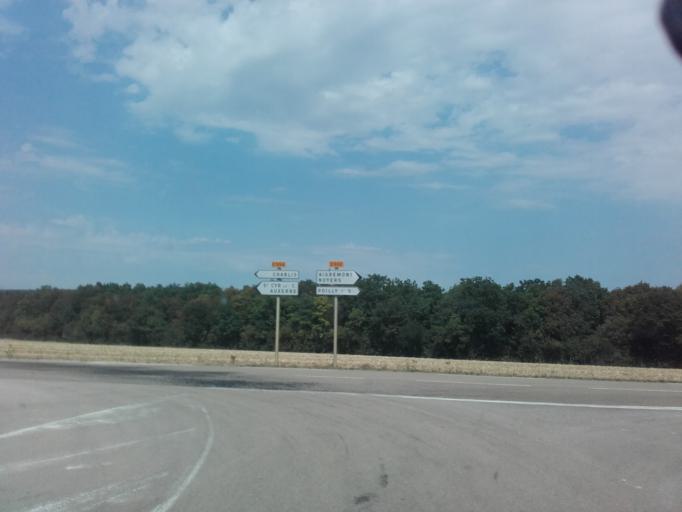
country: FR
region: Bourgogne
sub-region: Departement de l'Yonne
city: Chablis
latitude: 47.7305
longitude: 3.8513
